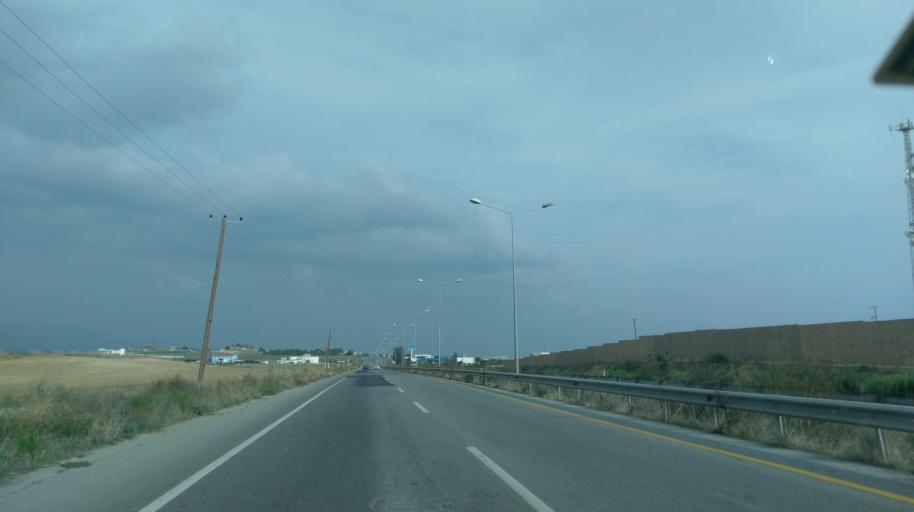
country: CY
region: Lefkosia
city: Mammari
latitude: 35.2117
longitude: 33.2383
